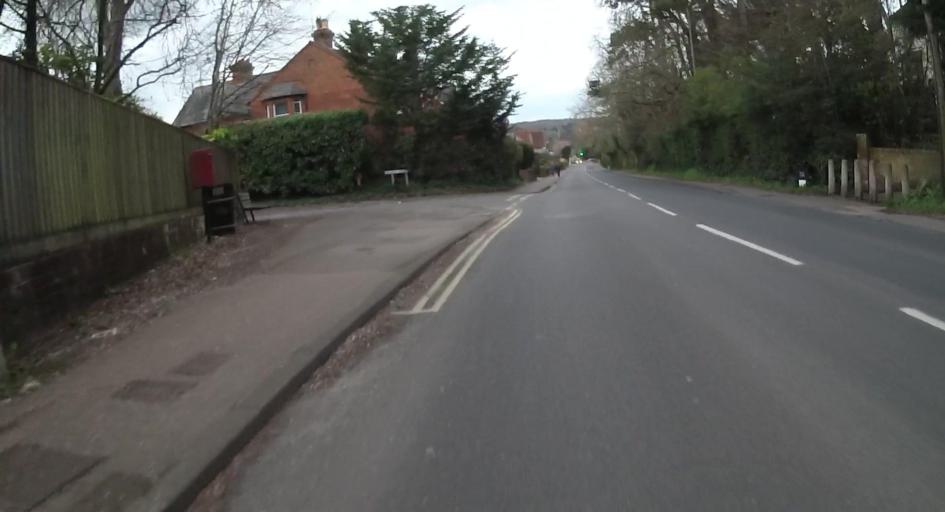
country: GB
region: England
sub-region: Surrey
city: Farnham
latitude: 51.2070
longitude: -0.7949
